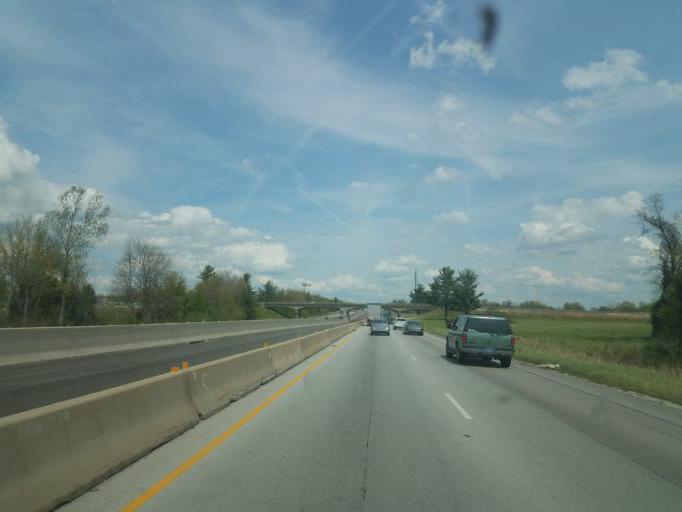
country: US
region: Kentucky
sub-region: Hardin County
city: Elizabethtown
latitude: 37.5940
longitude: -85.8690
